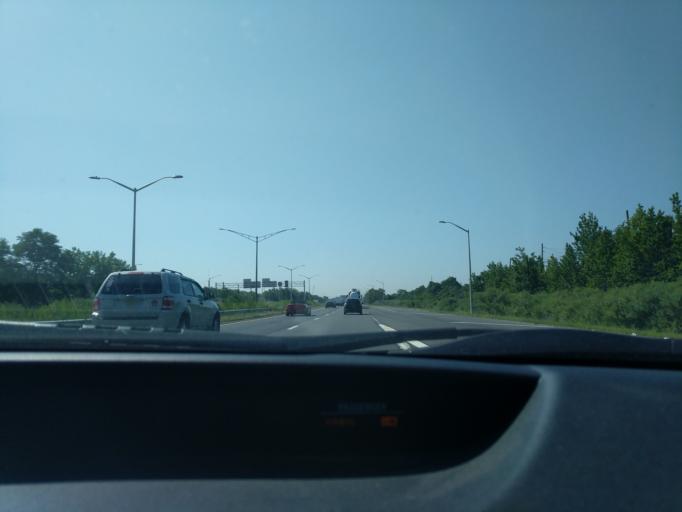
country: US
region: New York
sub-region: Richmond County
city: Bloomfield
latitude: 40.5867
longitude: -74.1929
